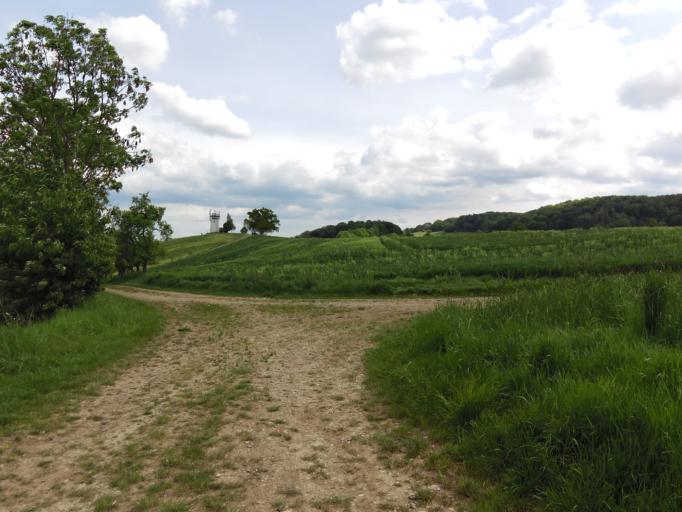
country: DE
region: Thuringia
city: Ifta
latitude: 51.0586
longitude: 10.1668
